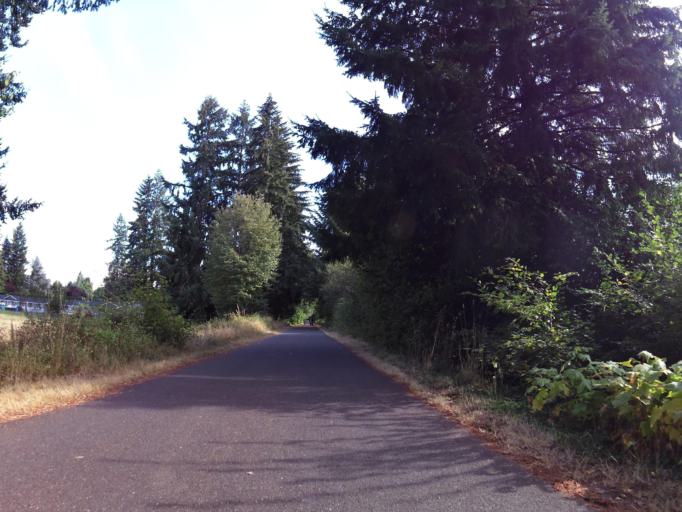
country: US
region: Washington
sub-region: Thurston County
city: Lacey
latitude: 47.0310
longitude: -122.8378
